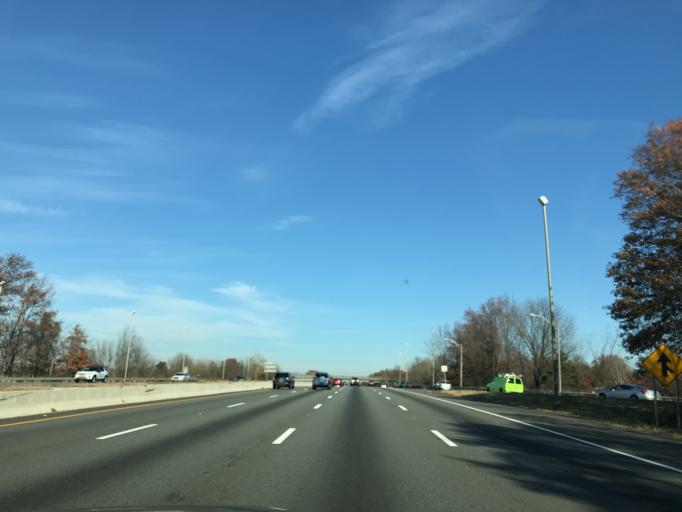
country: US
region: New Jersey
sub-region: Morris County
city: Parsippany
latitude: 40.8309
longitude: -74.4393
